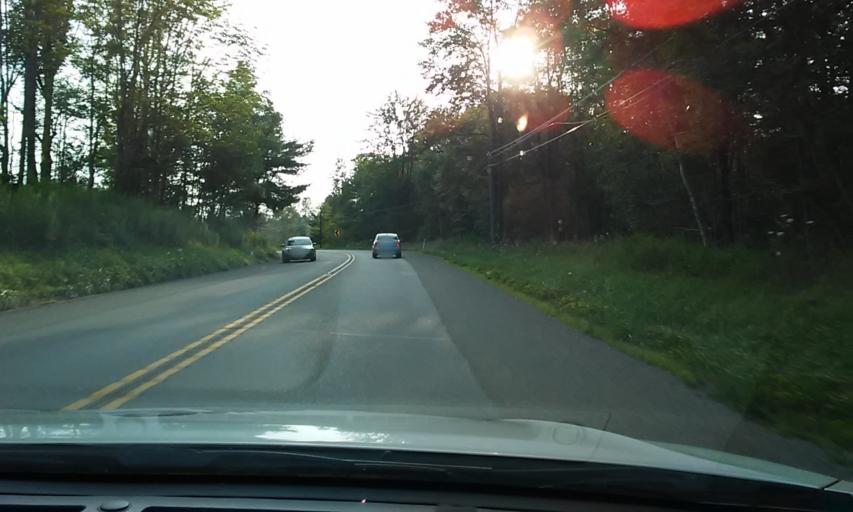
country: US
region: Pennsylvania
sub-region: McKean County
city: Kane
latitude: 41.6991
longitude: -78.7112
